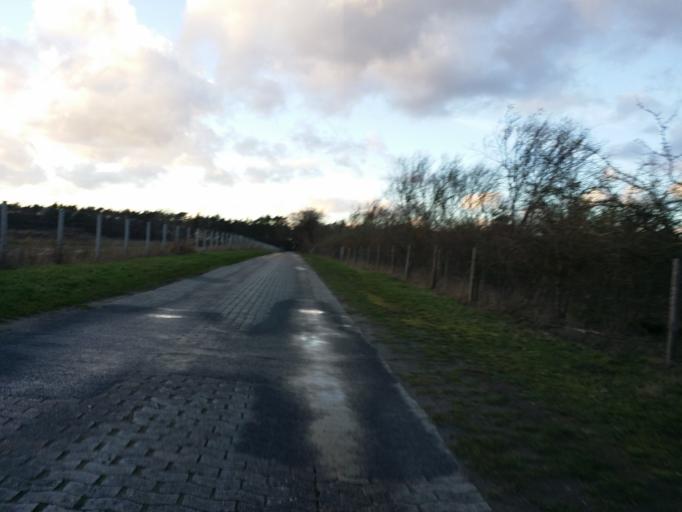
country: DE
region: Lower Saxony
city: Gross Ippener
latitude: 52.9631
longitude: 8.6019
